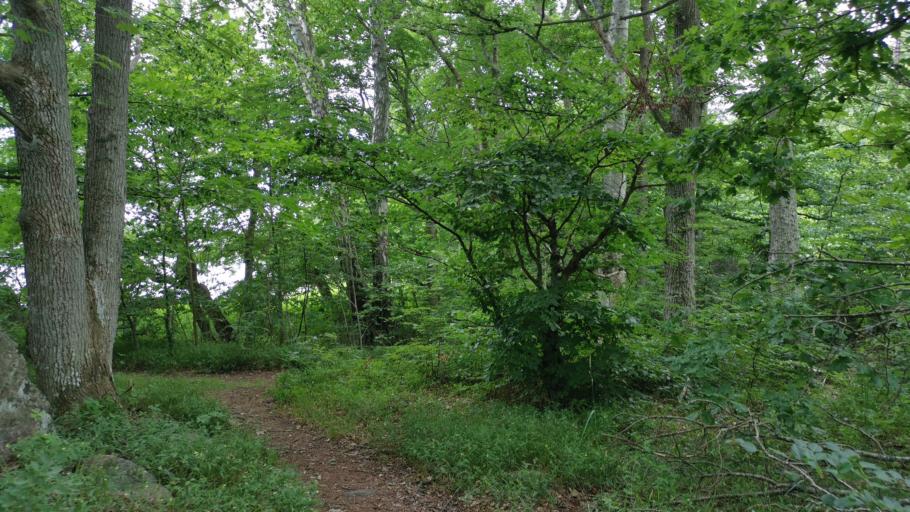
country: SE
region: Vaestra Goetaland
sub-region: Lysekils Kommun
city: Lysekil
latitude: 58.2408
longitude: 11.4895
